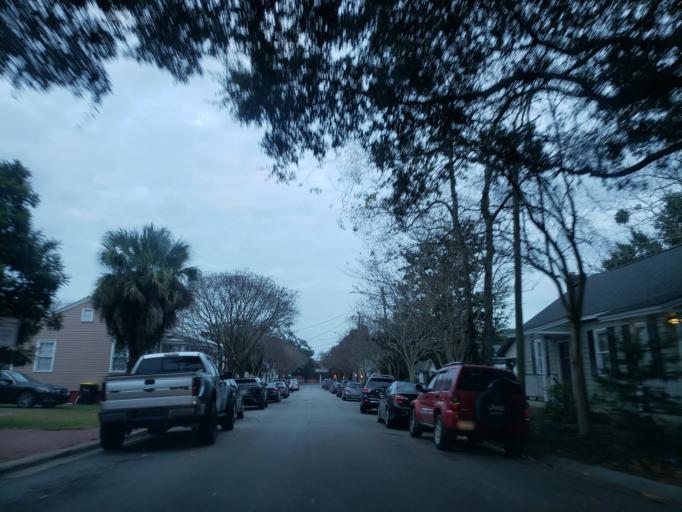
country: US
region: Georgia
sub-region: Chatham County
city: Savannah
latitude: 32.0718
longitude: -81.0883
